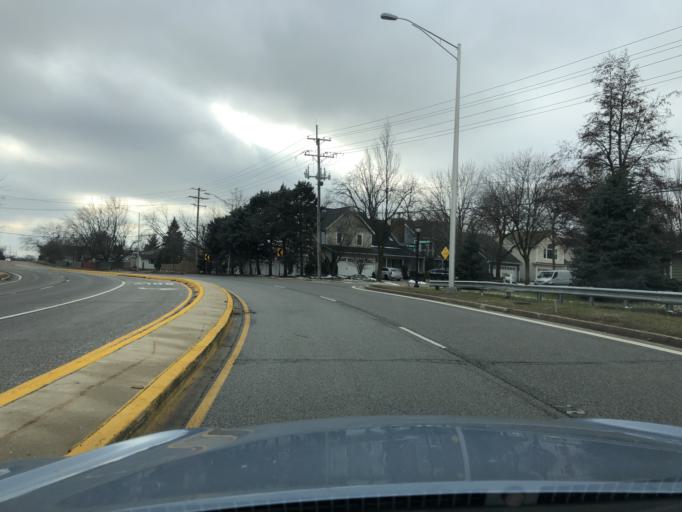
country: US
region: Illinois
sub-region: Cook County
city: Elk Grove Village
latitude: 42.0117
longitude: -88.0031
